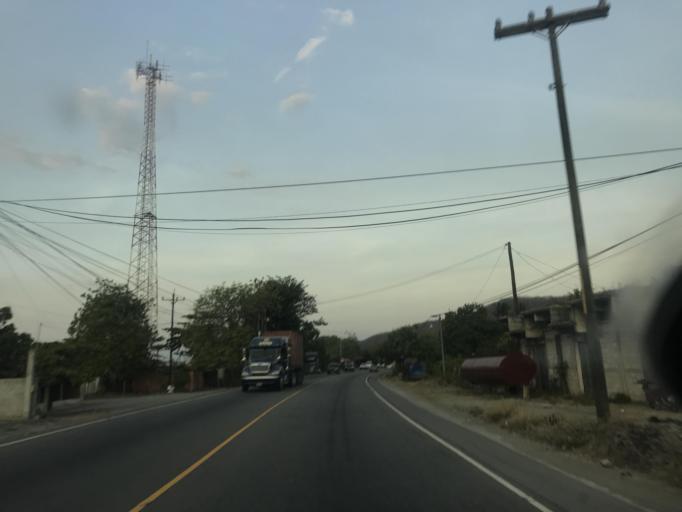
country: GT
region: Zacapa
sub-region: Municipio de Zacapa
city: Gualan
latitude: 15.0868
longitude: -89.4648
